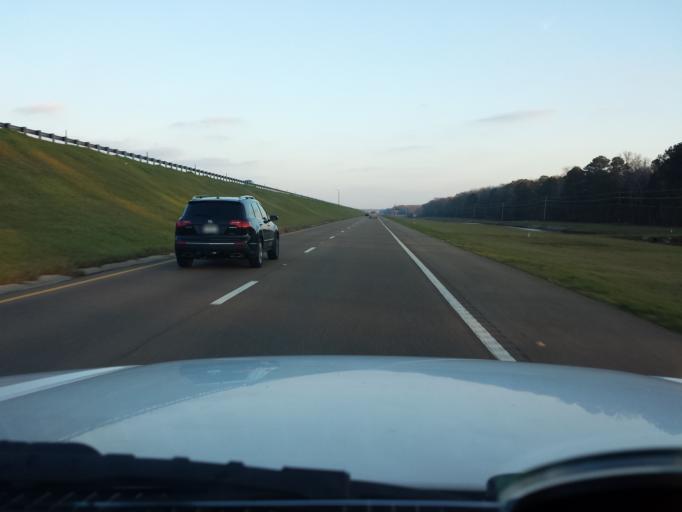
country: US
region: Mississippi
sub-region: Madison County
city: Ridgeland
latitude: 32.4056
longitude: -90.0778
